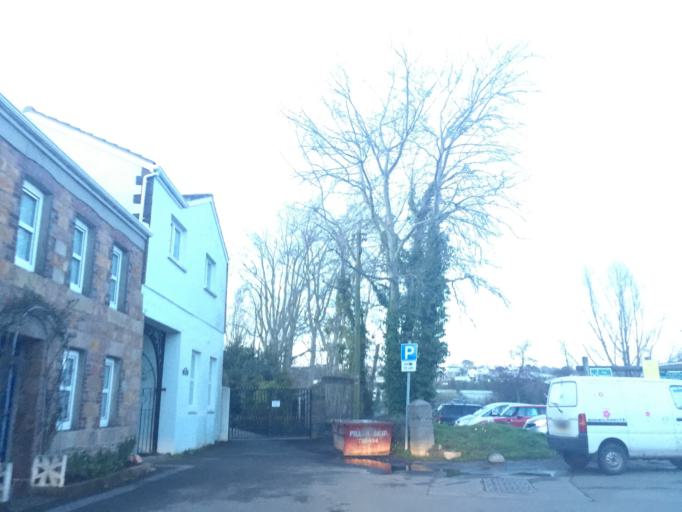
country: JE
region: St Helier
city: Saint Helier
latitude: 49.1975
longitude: -2.1594
